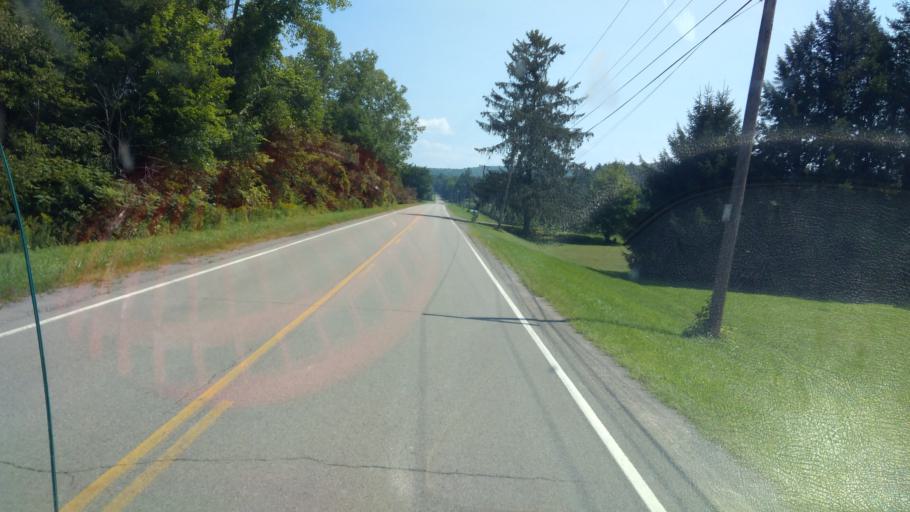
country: US
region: New York
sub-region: Allegany County
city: Belmont
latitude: 42.3004
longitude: -77.9867
